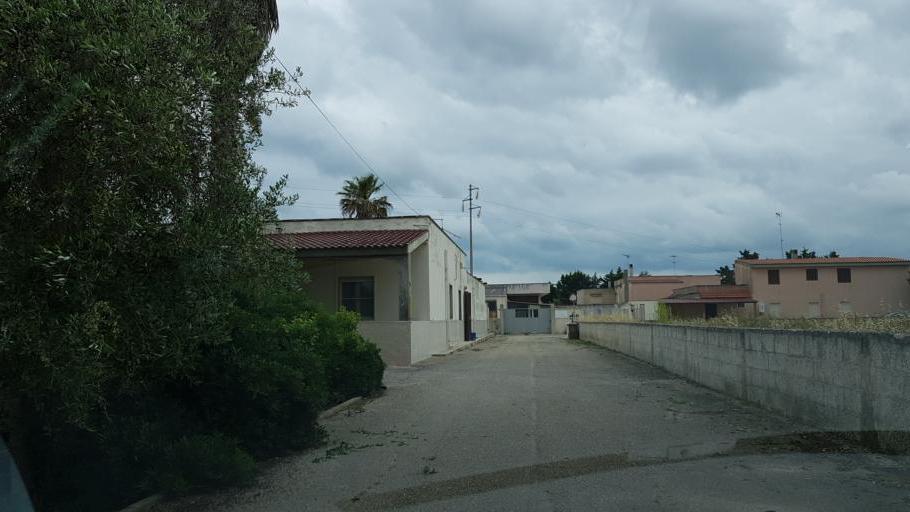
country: IT
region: Apulia
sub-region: Provincia di Brindisi
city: Brindisi
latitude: 40.6356
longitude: 17.8760
